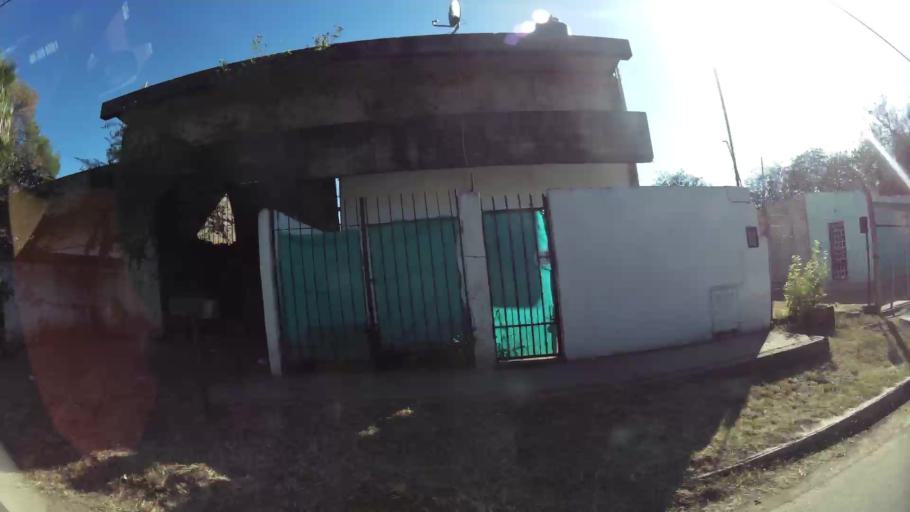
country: AR
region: Cordoba
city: Villa Allende
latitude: -31.3310
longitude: -64.2602
